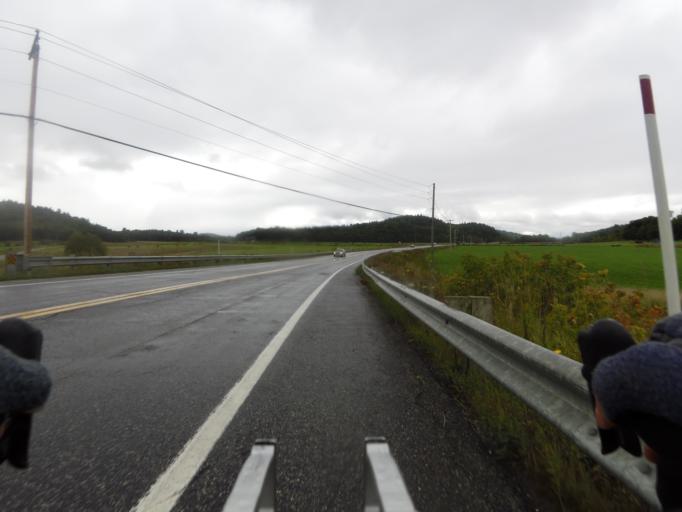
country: CA
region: Quebec
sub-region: Outaouais
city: Wakefield
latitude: 45.6446
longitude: -75.8902
